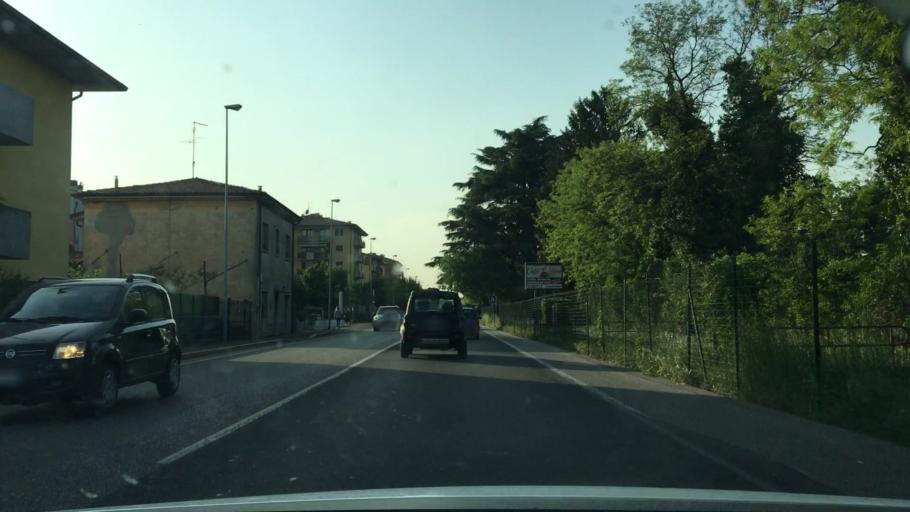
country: IT
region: Veneto
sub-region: Provincia di Verona
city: Verona
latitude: 45.4086
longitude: 11.0058
